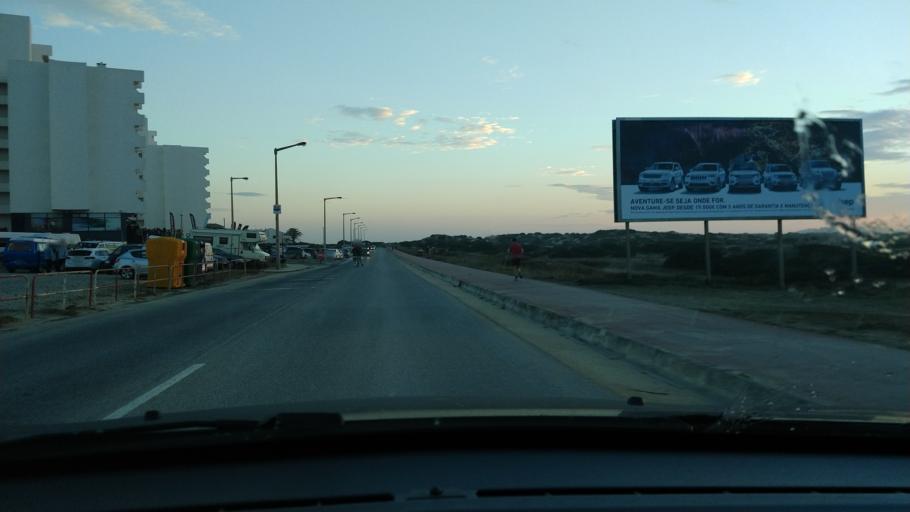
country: PT
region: Leiria
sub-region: Peniche
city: Atouguia da Baleia
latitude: 39.3661
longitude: -9.3370
